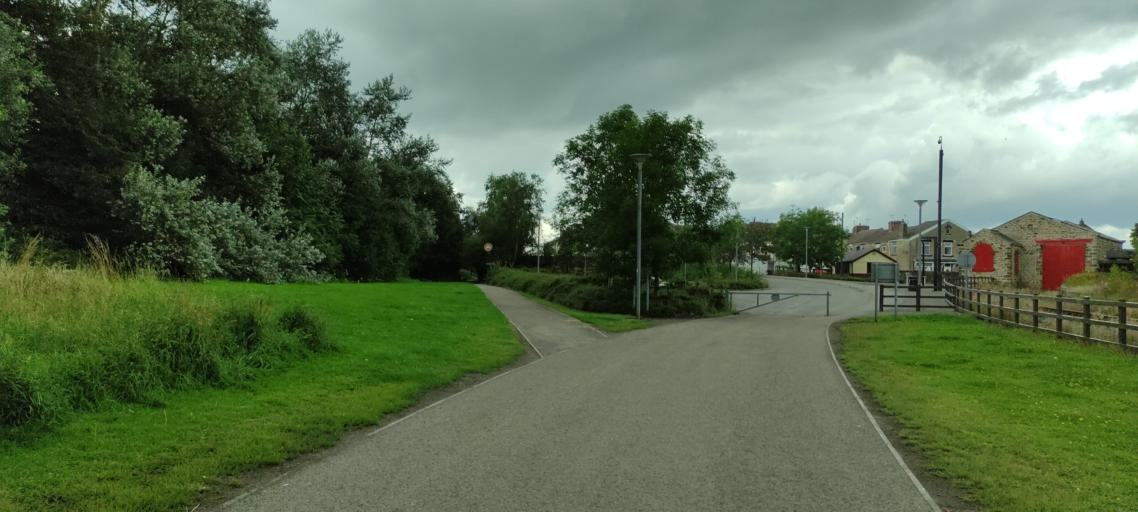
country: GB
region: England
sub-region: County Durham
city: Shildon
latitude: 54.6262
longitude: -1.6402
